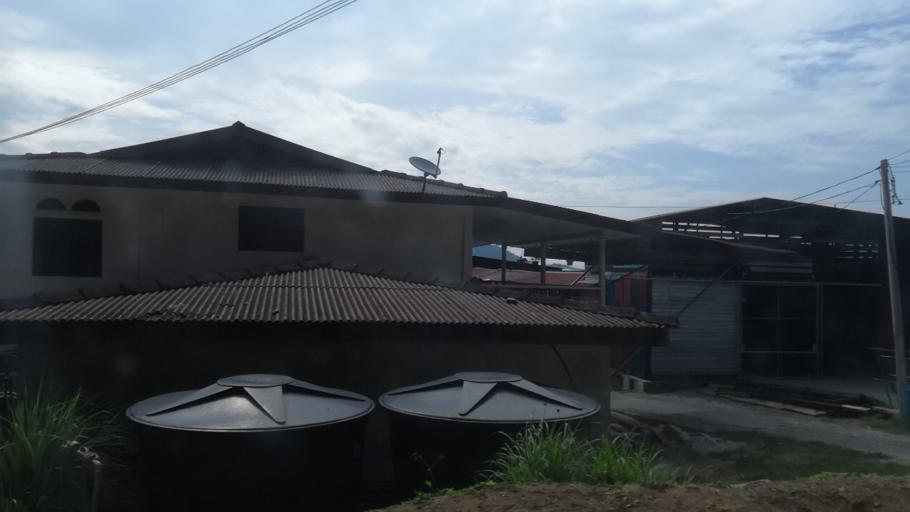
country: MY
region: Perak
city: Lumut
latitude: 4.2171
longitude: 100.5758
